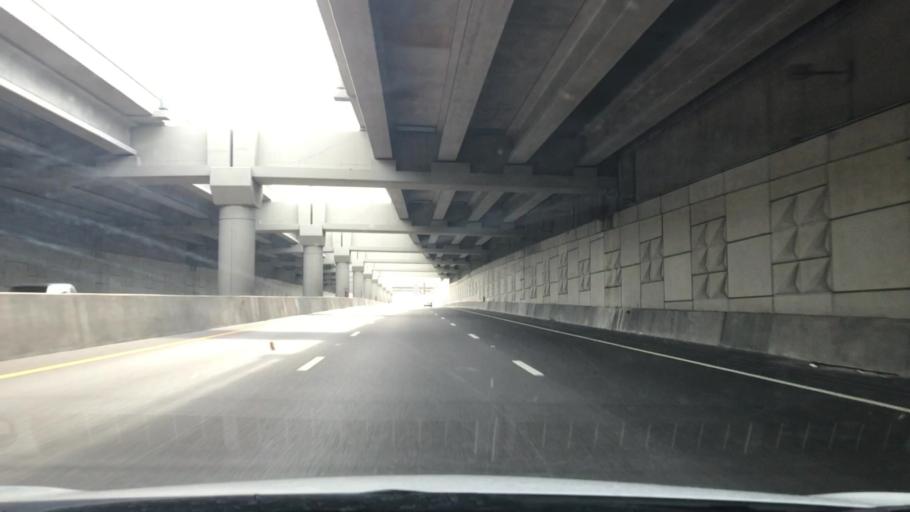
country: US
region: Texas
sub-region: Dallas County
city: Addison
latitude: 32.9249
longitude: -96.8123
